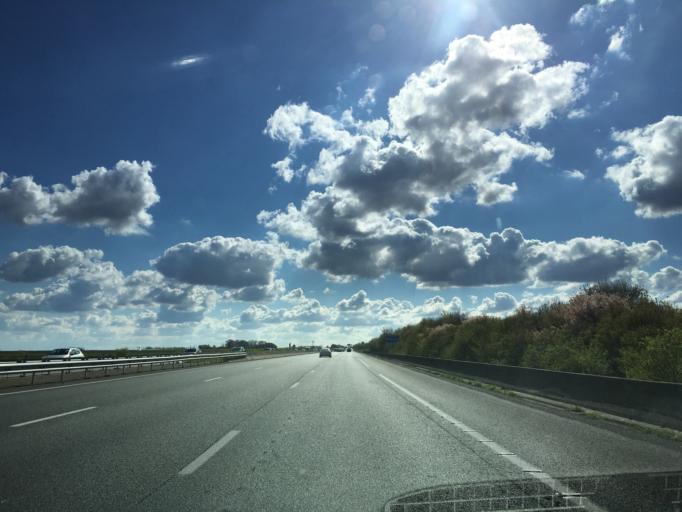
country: FR
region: Nord-Pas-de-Calais
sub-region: Departement du Pas-de-Calais
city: Vitry-en-Artois
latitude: 50.3529
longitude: 2.9501
